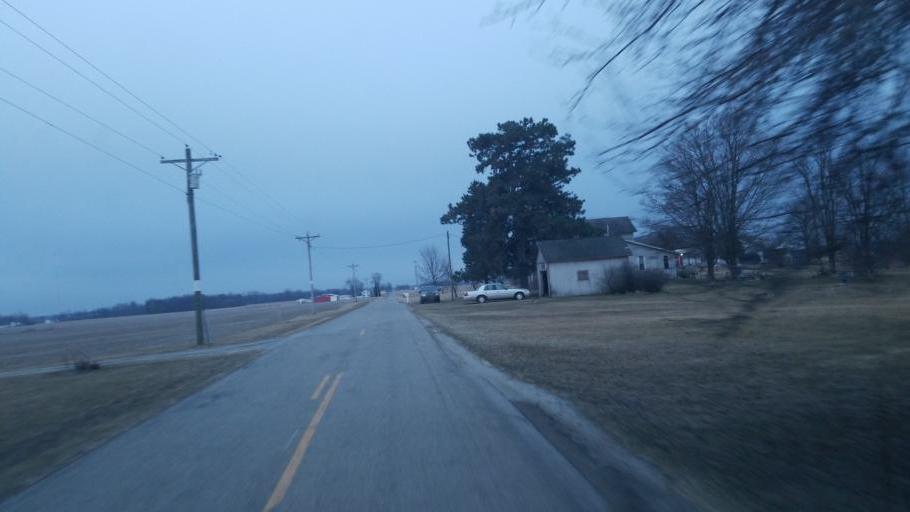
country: US
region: Ohio
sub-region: Defiance County
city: Hicksville
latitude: 41.3352
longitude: -84.7286
